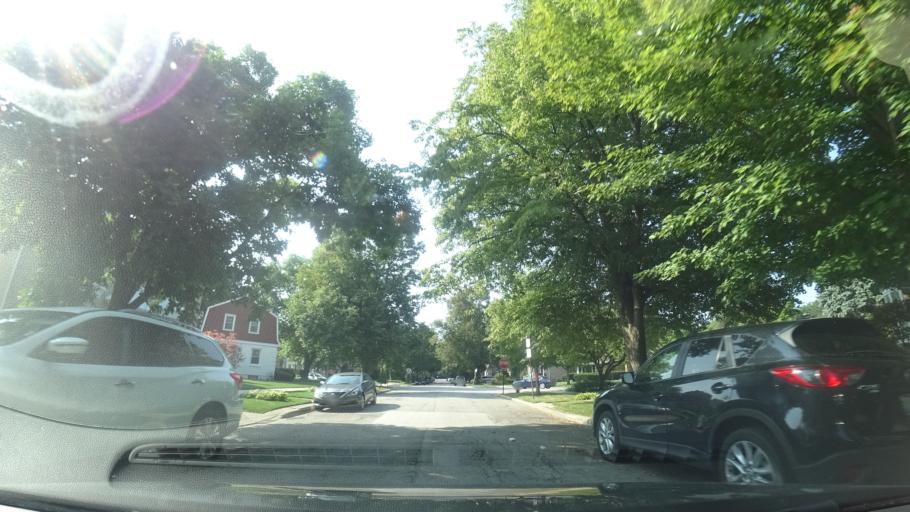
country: US
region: Illinois
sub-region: Cook County
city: Lincolnwood
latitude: 41.9888
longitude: -87.7472
